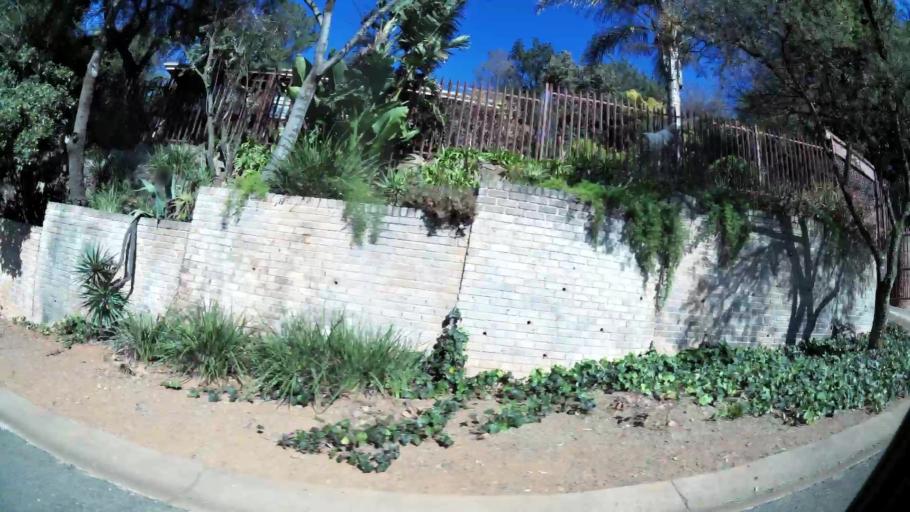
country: ZA
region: Gauteng
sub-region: City of Johannesburg Metropolitan Municipality
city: Roodepoort
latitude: -26.1221
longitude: 27.8724
